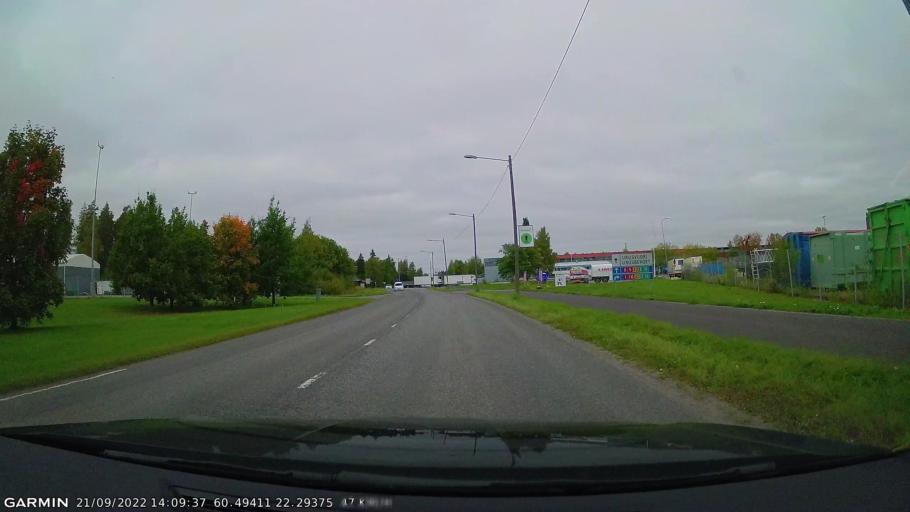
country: FI
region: Varsinais-Suomi
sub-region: Turku
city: Turku
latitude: 60.4942
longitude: 22.2938
